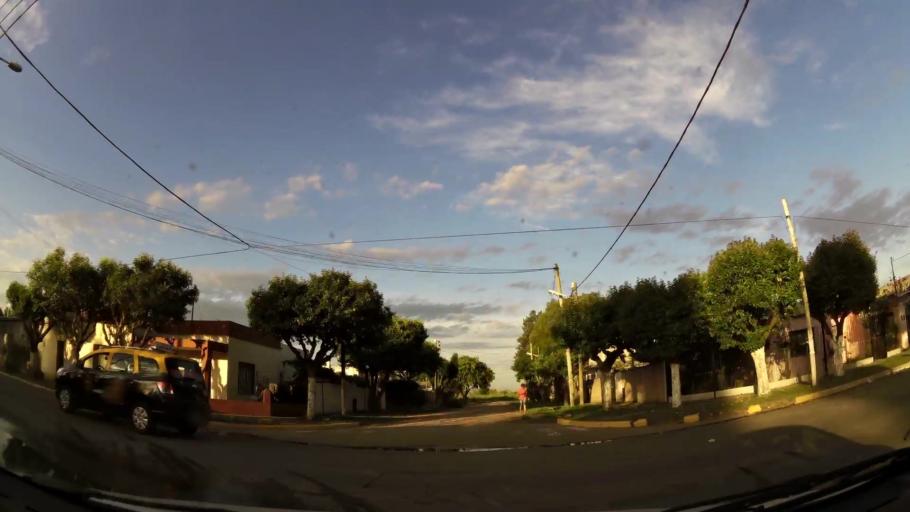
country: AR
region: Buenos Aires
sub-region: Partido de Merlo
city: Merlo
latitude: -34.6771
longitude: -58.7519
